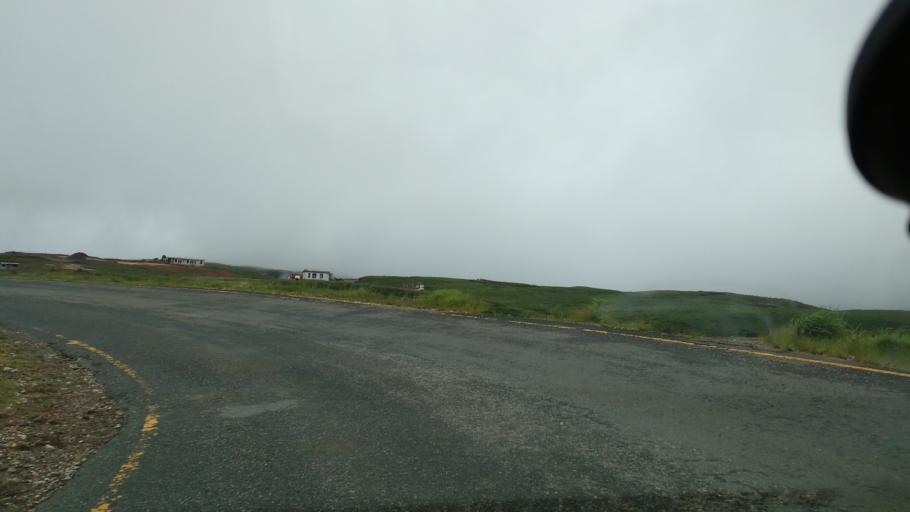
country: IN
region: Meghalaya
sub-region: East Khasi Hills
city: Cherrapunji
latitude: 25.3220
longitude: 91.7327
